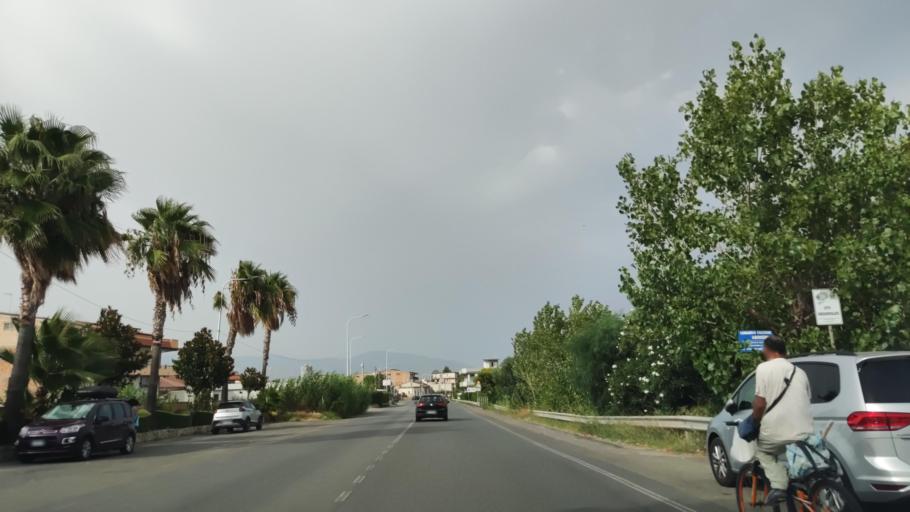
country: IT
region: Calabria
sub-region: Provincia di Reggio Calabria
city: Siderno
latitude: 38.2548
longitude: 16.2828
